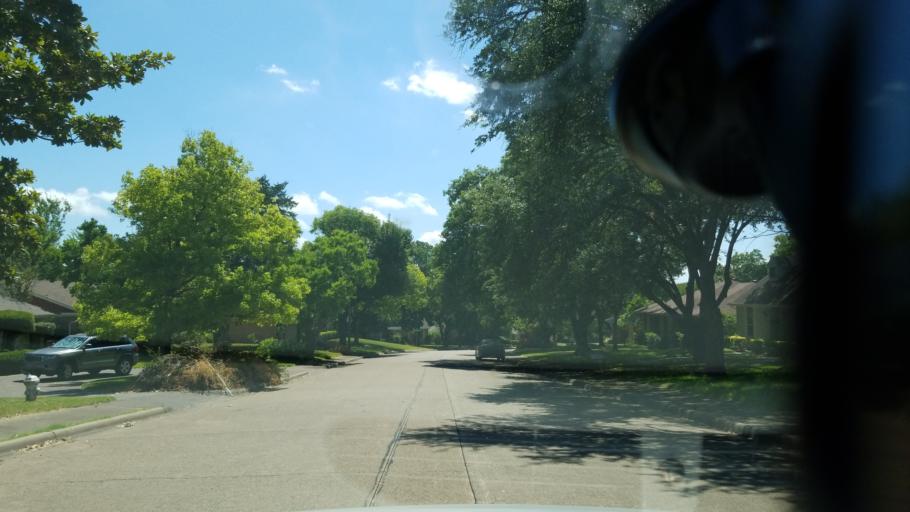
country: US
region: Texas
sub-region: Dallas County
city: Cockrell Hill
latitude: 32.6816
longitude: -96.8328
